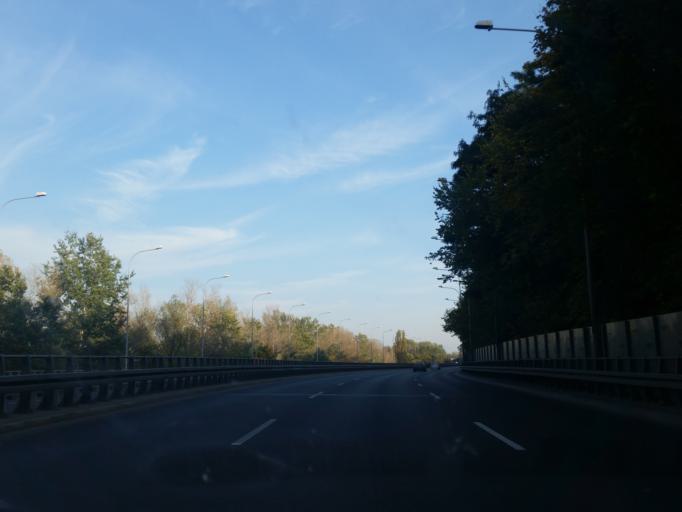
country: PL
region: Masovian Voivodeship
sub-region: Warszawa
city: Bielany
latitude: 52.2994
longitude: 20.9572
